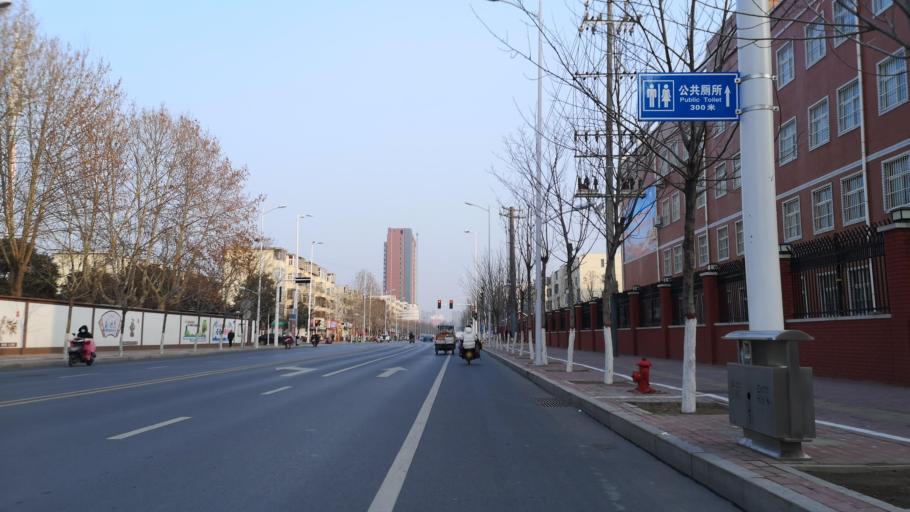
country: CN
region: Henan Sheng
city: Zhongyuanlu
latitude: 35.7633
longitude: 115.0613
